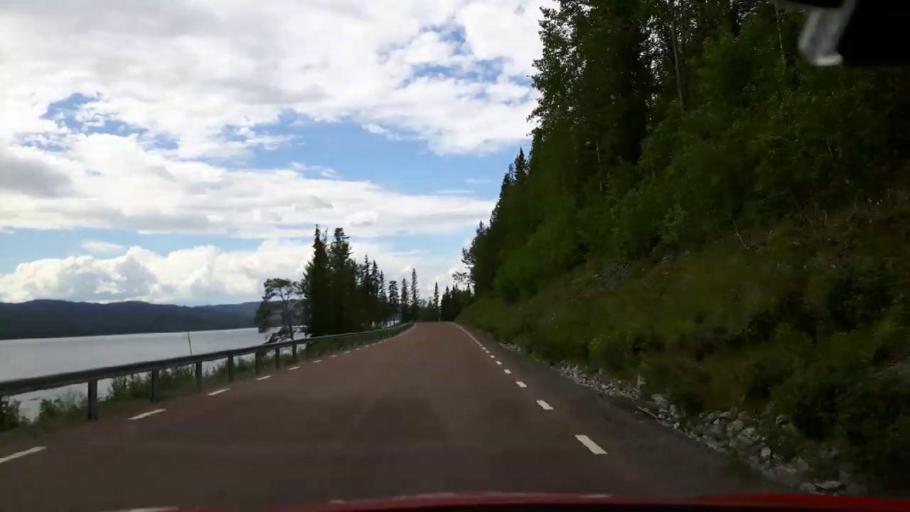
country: SE
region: Jaemtland
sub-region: Krokoms Kommun
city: Valla
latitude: 64.0863
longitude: 14.0654
